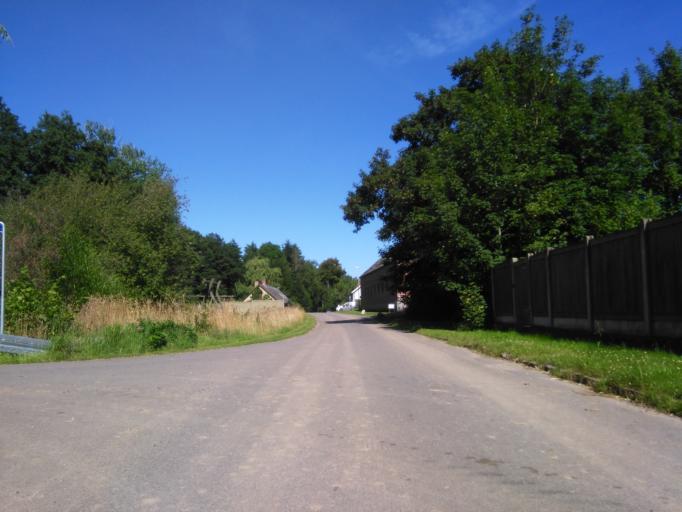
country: DK
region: Central Jutland
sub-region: Odder Kommune
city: Odder
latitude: 55.9619
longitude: 10.1042
